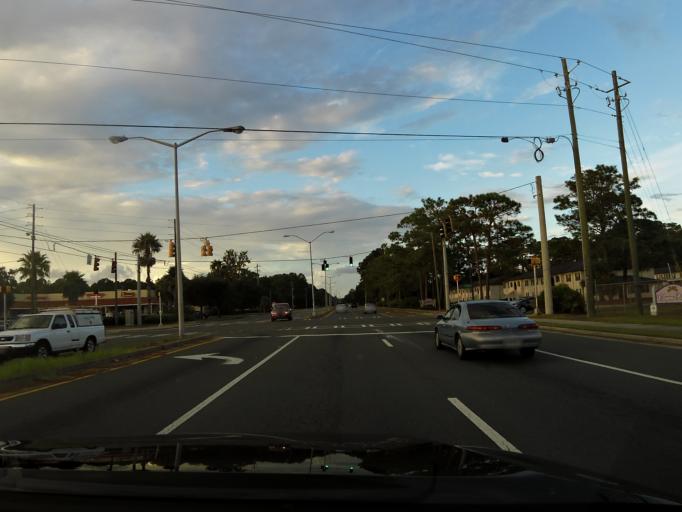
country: US
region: Georgia
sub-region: Glynn County
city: Country Club Estates
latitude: 31.2143
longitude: -81.4804
